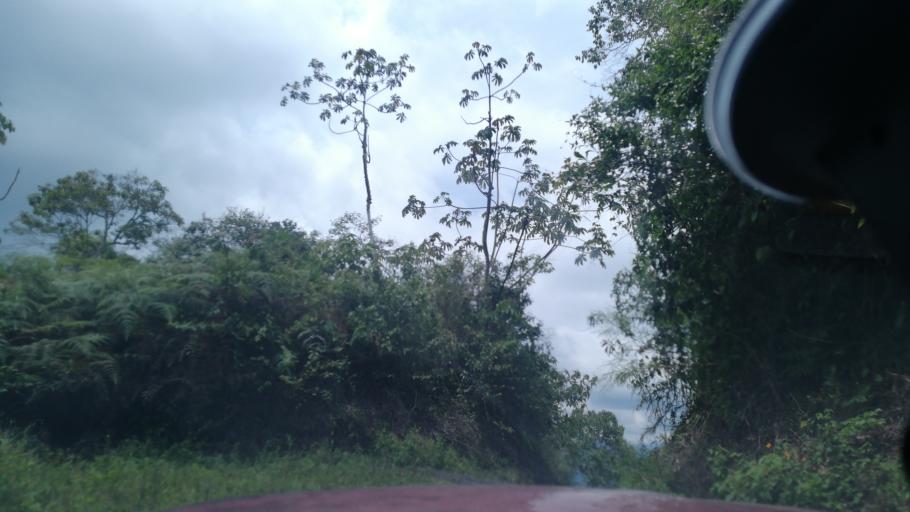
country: CO
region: Cundinamarca
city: Vergara
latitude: 5.1958
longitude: -74.2952
